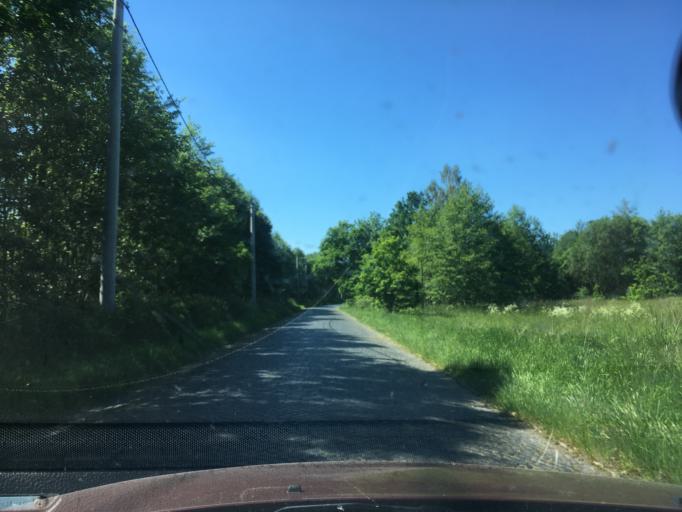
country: PL
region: Silesian Voivodeship
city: Zawidow
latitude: 51.0225
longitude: 15.0448
